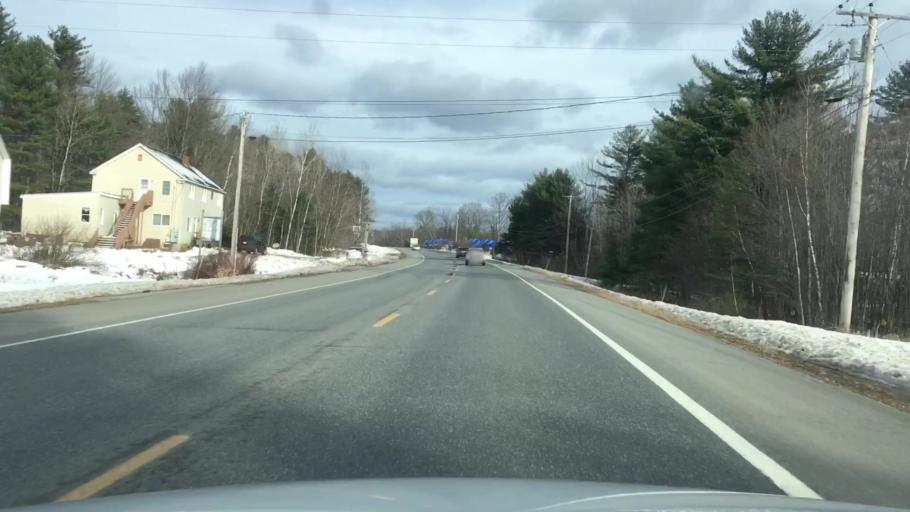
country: US
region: Maine
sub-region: Kennebec County
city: Monmouth
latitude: 44.2703
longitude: -70.0156
